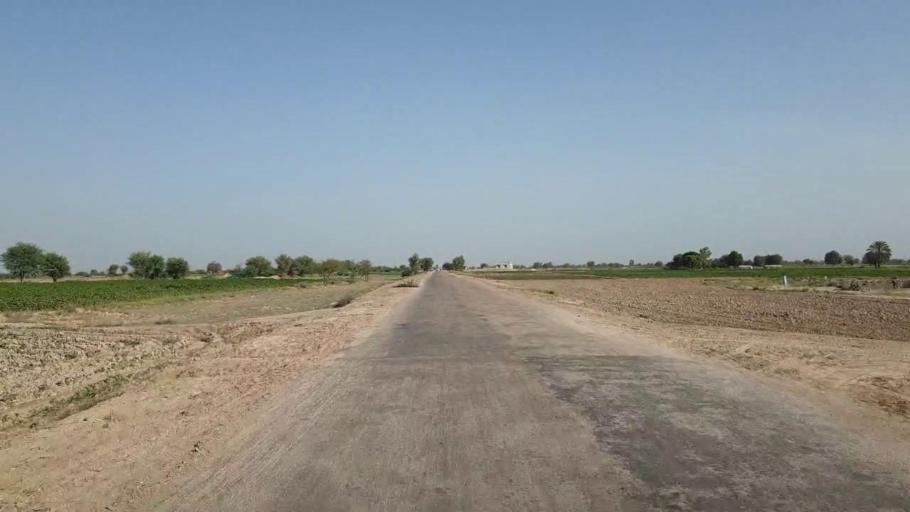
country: PK
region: Sindh
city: Nawabshah
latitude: 26.1451
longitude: 68.4502
